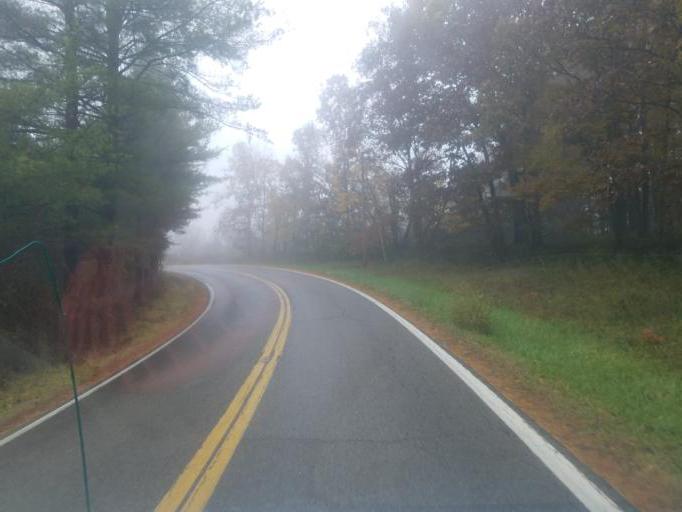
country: US
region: Ohio
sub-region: Morgan County
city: McConnelsville
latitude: 39.5388
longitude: -81.8012
